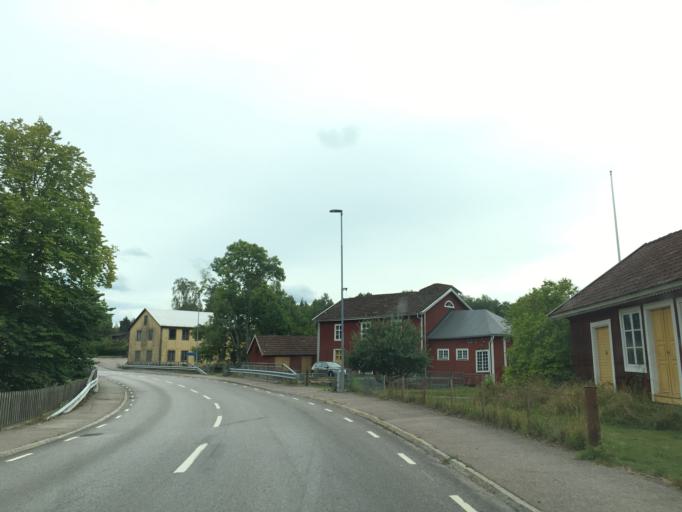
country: SE
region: Kalmar
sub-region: Nybro Kommun
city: Nybro
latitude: 56.9374
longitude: 15.9123
